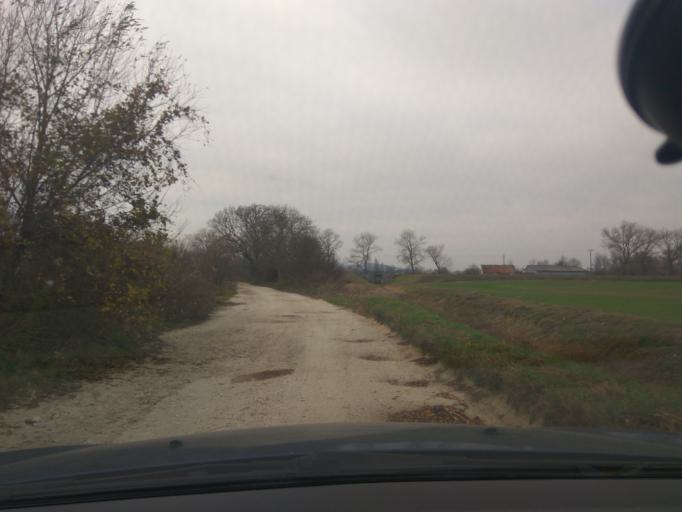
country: SK
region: Trnavsky
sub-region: Okres Trnava
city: Piestany
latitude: 48.6098
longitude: 17.8609
